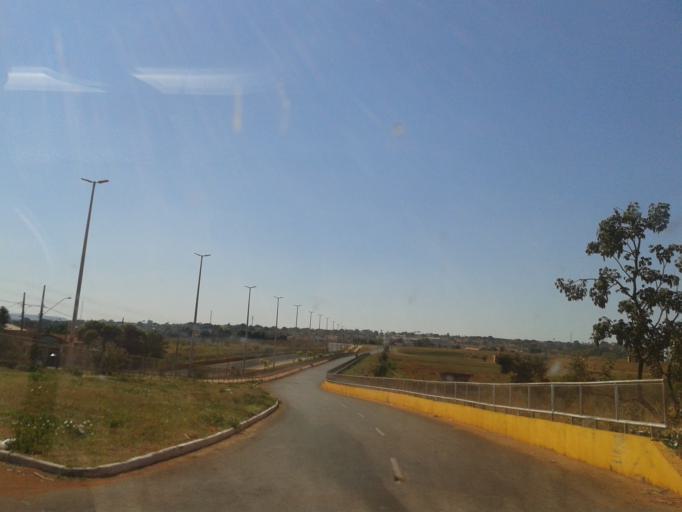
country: BR
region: Minas Gerais
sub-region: Ituiutaba
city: Ituiutaba
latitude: -19.0028
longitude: -49.4788
